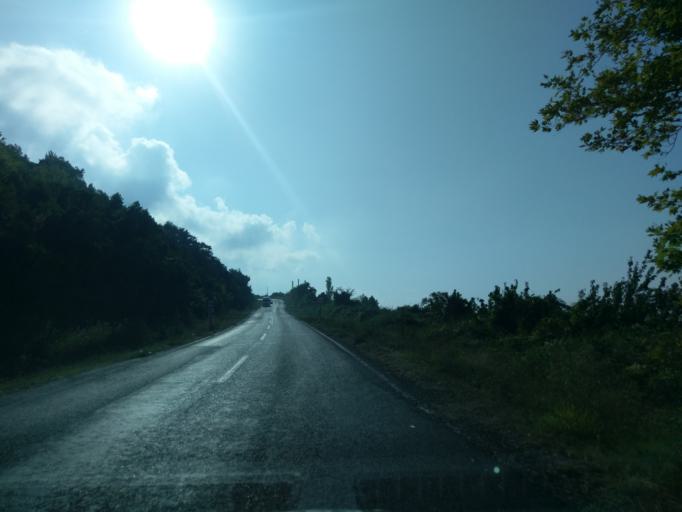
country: TR
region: Sinop
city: Ayancik
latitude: 41.9429
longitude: 34.6825
